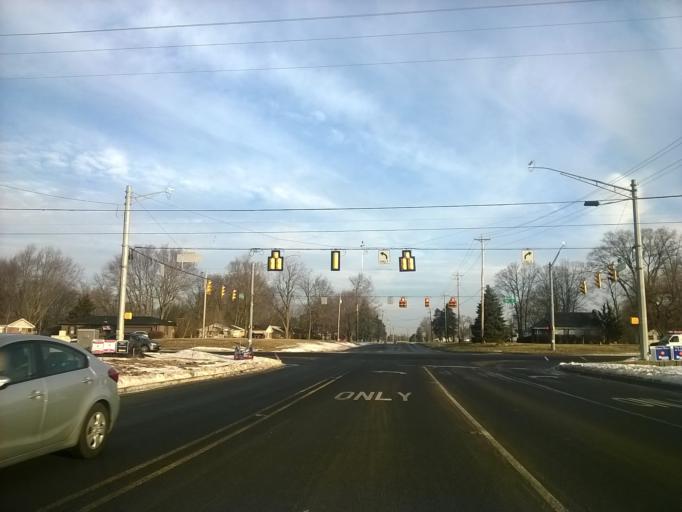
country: US
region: Indiana
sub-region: Hamilton County
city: Fishers
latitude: 39.9995
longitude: -86.0338
